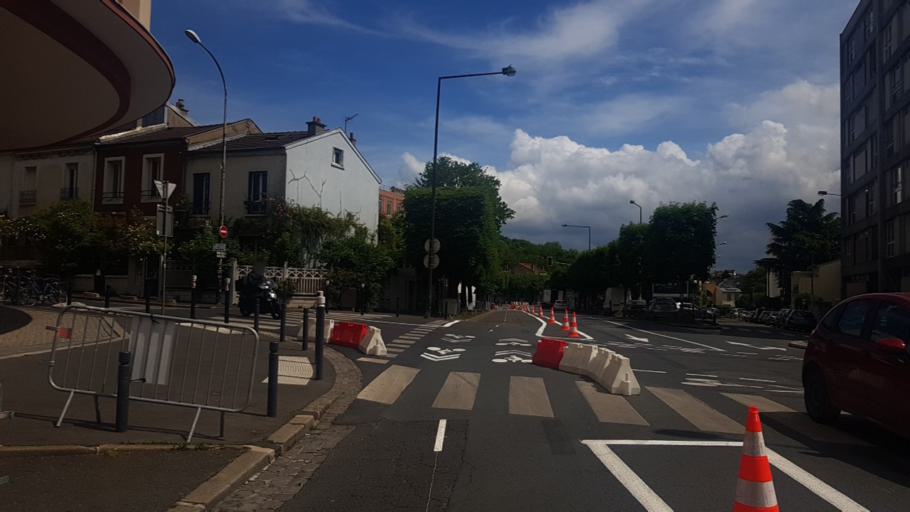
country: FR
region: Ile-de-France
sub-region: Departement de Seine-Saint-Denis
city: Montreuil
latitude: 48.8569
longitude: 2.4428
